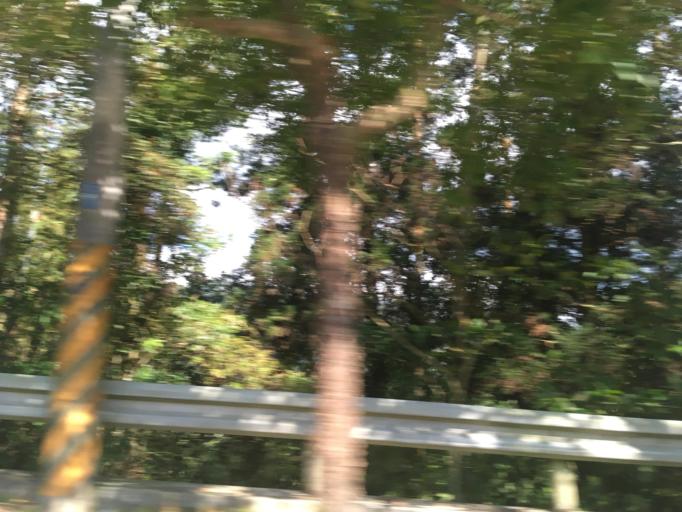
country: TW
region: Taiwan
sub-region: Yilan
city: Yilan
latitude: 24.7541
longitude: 121.6404
